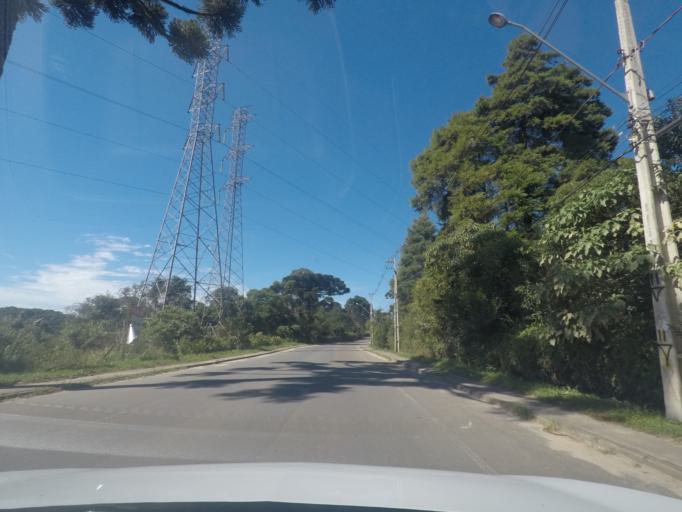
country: BR
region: Parana
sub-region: Almirante Tamandare
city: Almirante Tamandare
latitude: -25.3398
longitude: -49.3057
